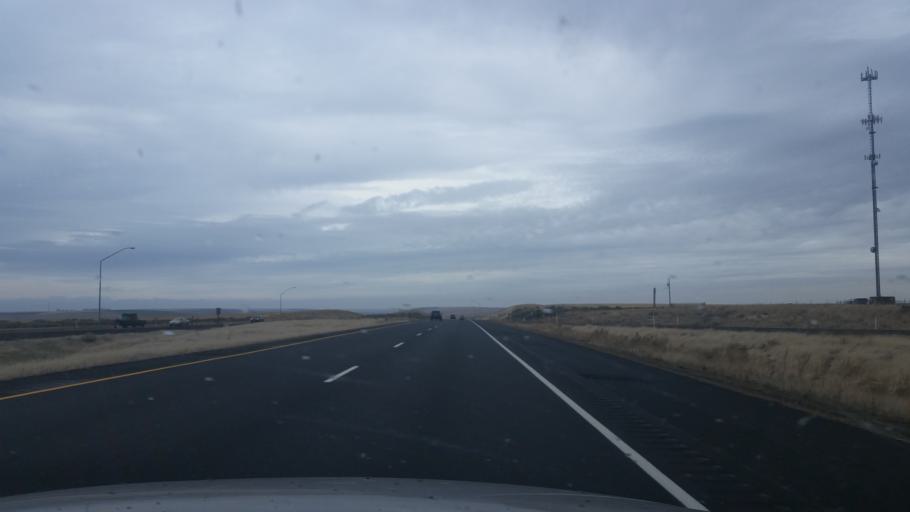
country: US
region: Washington
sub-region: Grant County
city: Warden
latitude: 47.0866
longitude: -118.8495
